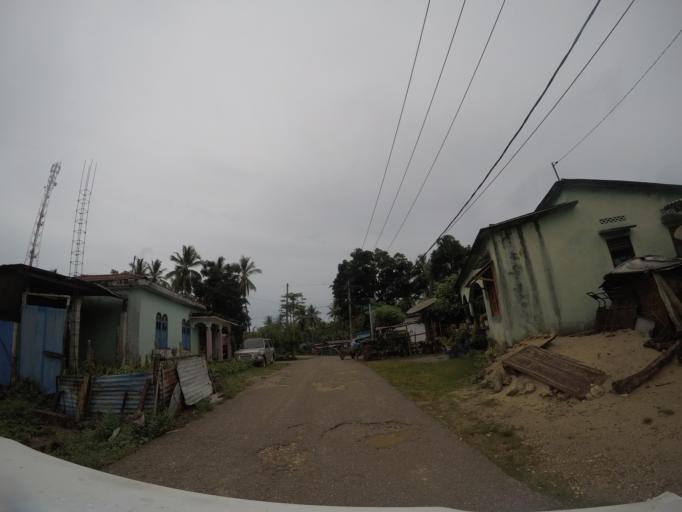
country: TL
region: Lautem
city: Lospalos
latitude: -8.5249
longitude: 126.9991
